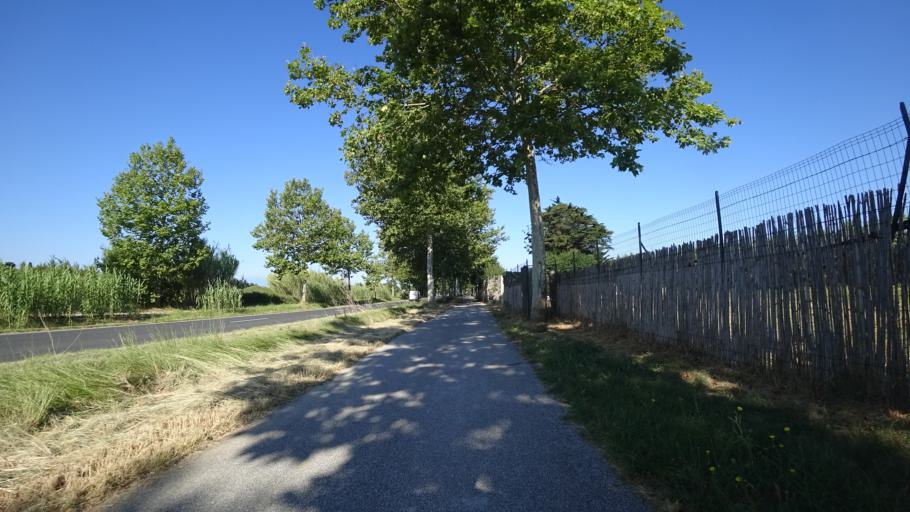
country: FR
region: Languedoc-Roussillon
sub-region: Departement des Pyrenees-Orientales
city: Villelongue-de-la-Salanque
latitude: 42.7273
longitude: 2.9984
